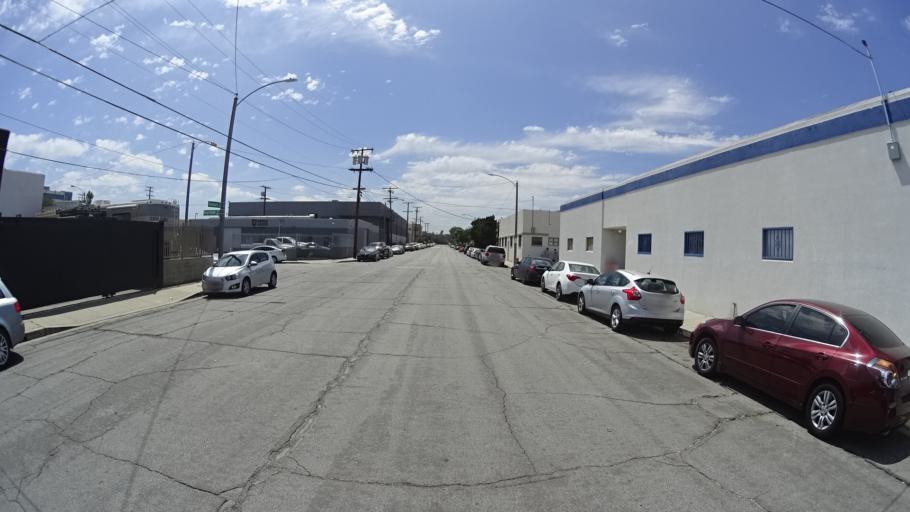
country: US
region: California
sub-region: Los Angeles County
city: Burbank
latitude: 34.1937
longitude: -118.3338
